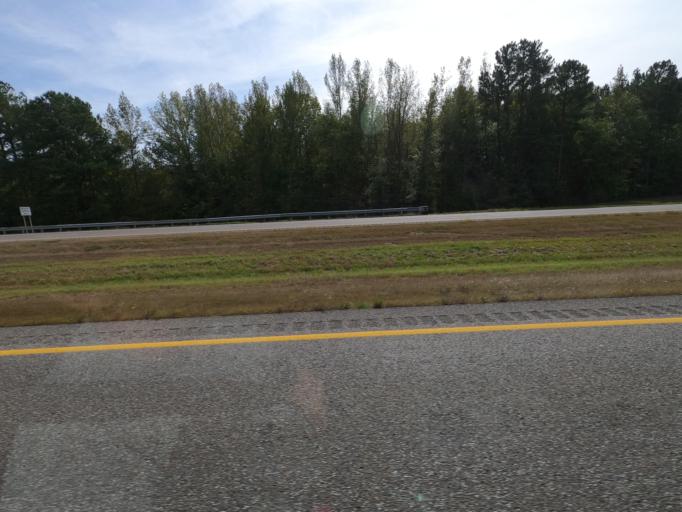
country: US
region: Tennessee
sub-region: Humphreys County
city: New Johnsonville
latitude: 35.8502
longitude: -88.0683
